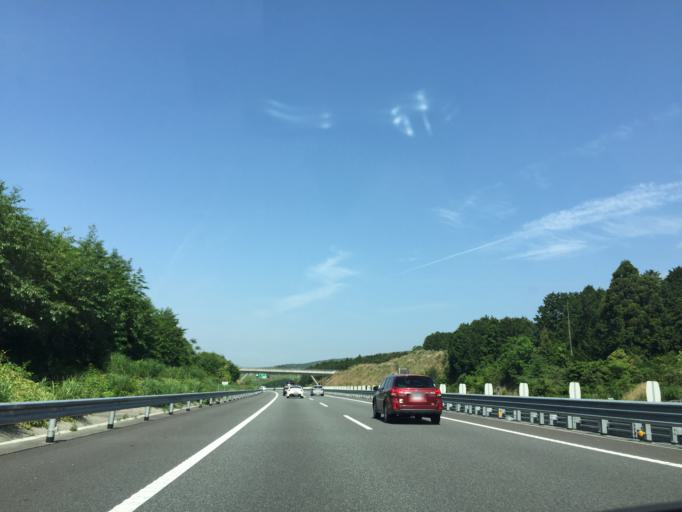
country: JP
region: Shizuoka
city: Numazu
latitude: 35.1539
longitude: 138.8351
